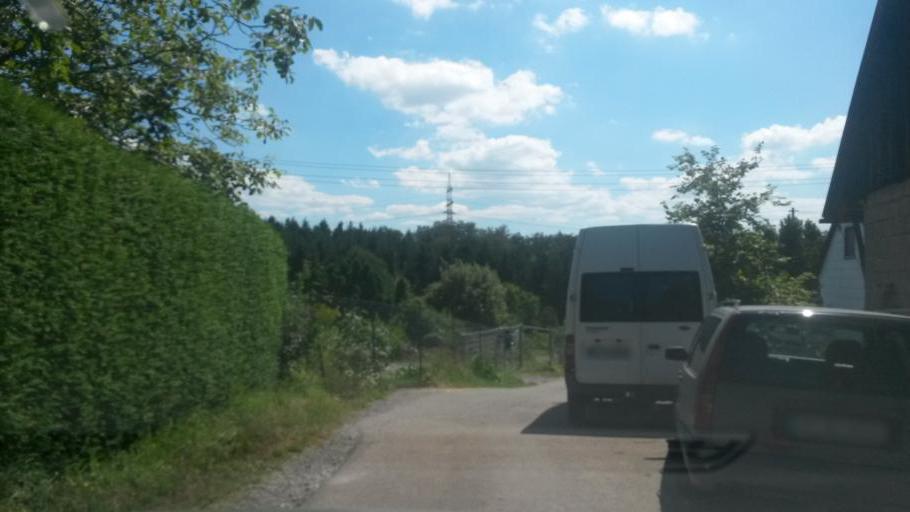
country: DE
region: Baden-Wuerttemberg
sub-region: Karlsruhe Region
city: Birkenfeld
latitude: 48.8927
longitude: 8.6345
